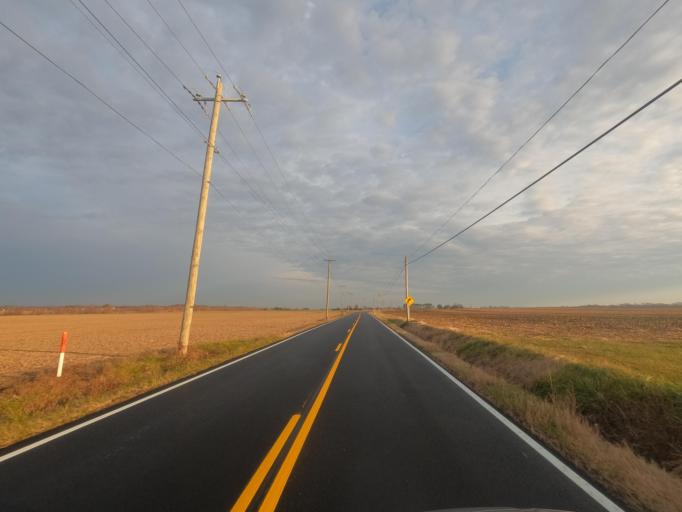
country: US
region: Delaware
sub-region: New Castle County
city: Townsend
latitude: 39.2836
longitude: -75.8365
